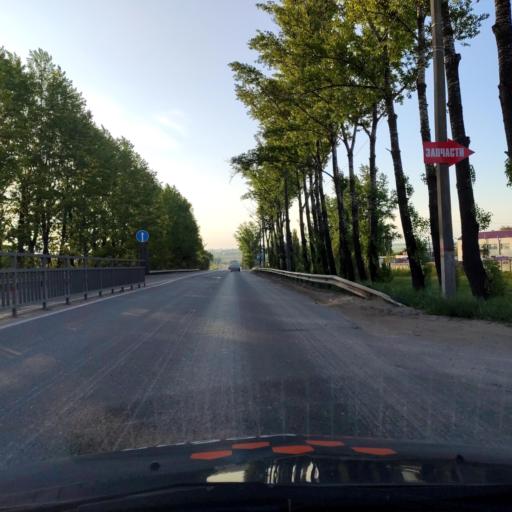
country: RU
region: Lipetsk
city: Yelets
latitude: 52.5941
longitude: 38.4844
